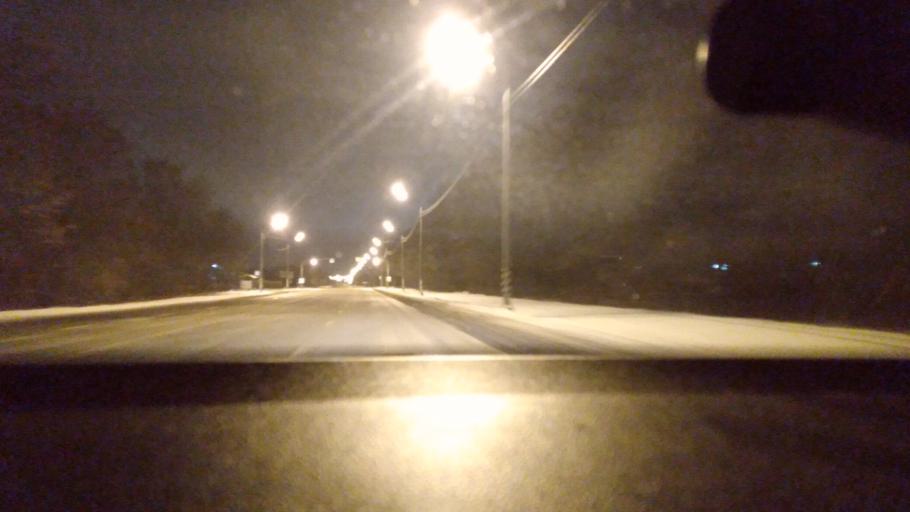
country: RU
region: Moskovskaya
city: Bronnitsy
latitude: 55.4769
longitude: 38.1843
